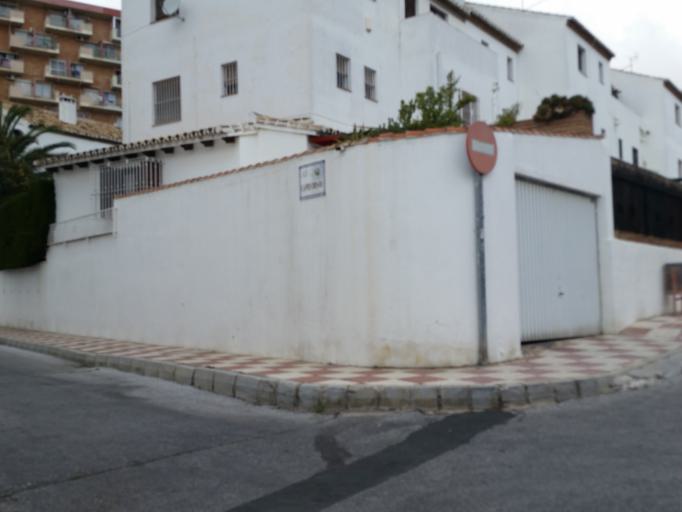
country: ES
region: Andalusia
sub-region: Provincia de Malaga
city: Torremolinos
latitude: 36.5953
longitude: -4.5250
